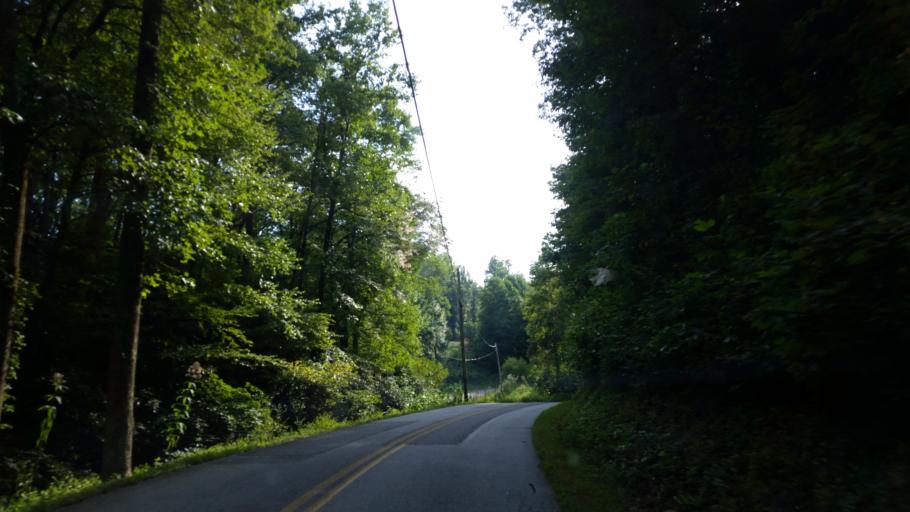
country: US
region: Georgia
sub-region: Lumpkin County
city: Dahlonega
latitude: 34.6681
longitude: -84.0333
